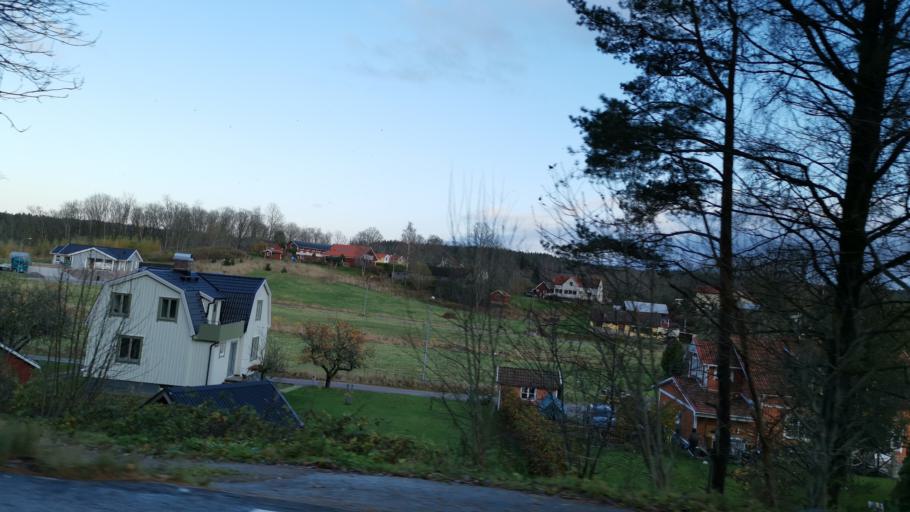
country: SE
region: Vaestra Goetaland
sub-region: Munkedals Kommun
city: Munkedal
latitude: 58.4881
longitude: 11.6938
